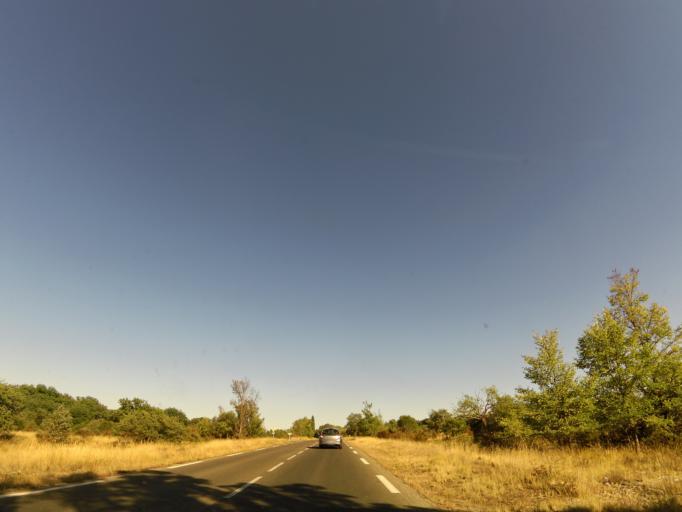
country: FR
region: Languedoc-Roussillon
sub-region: Departement du Gard
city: Saint-Hippolyte-du-Fort
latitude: 43.9496
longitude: 3.8850
